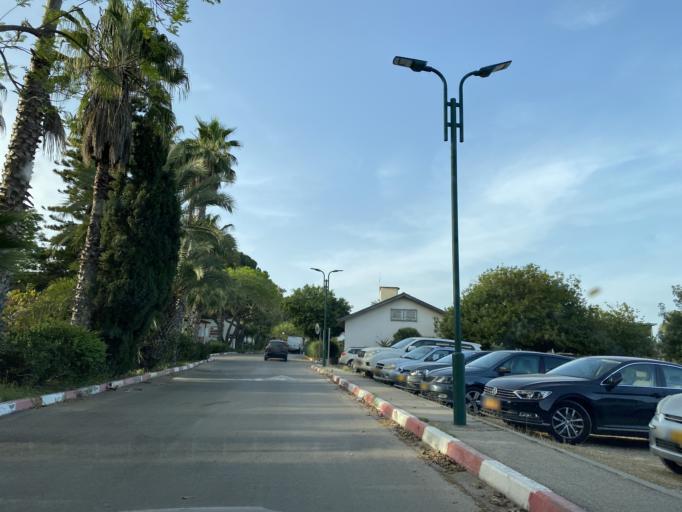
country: IL
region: Tel Aviv
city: Herzliyya
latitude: 32.1561
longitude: 34.8316
